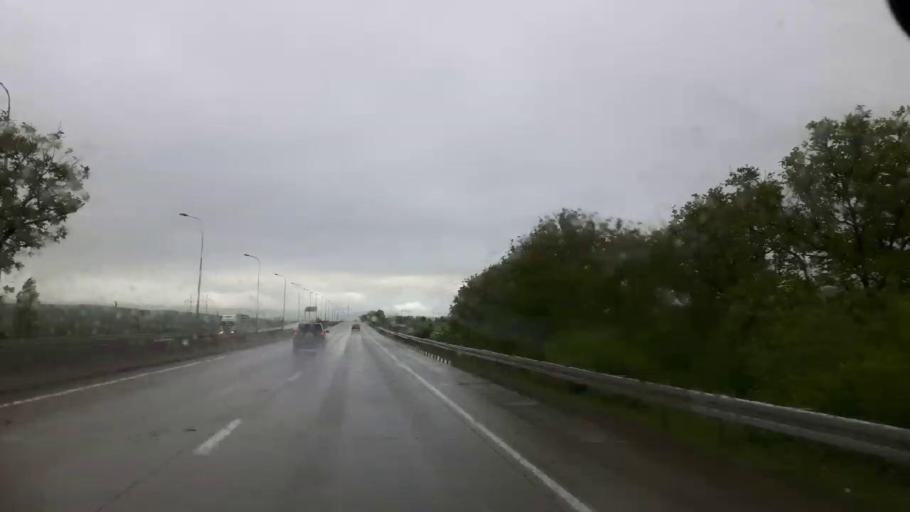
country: GE
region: Shida Kartli
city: Kaspi
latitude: 42.0198
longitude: 44.3095
